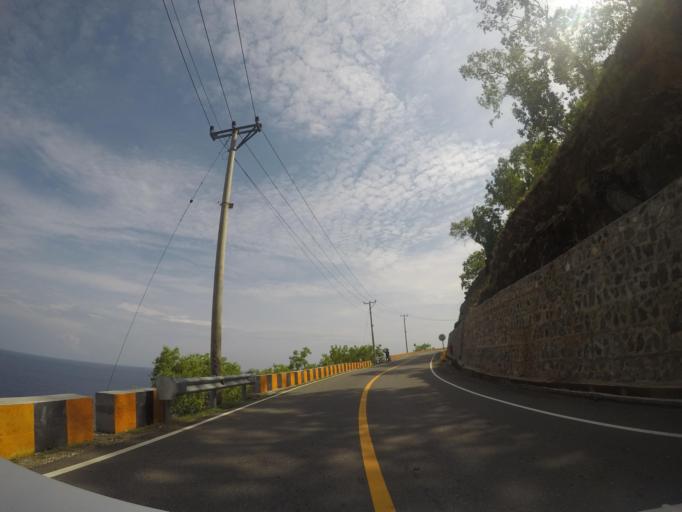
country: TL
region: Manatuto
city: Manatuto
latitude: -8.4764
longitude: 125.9001
